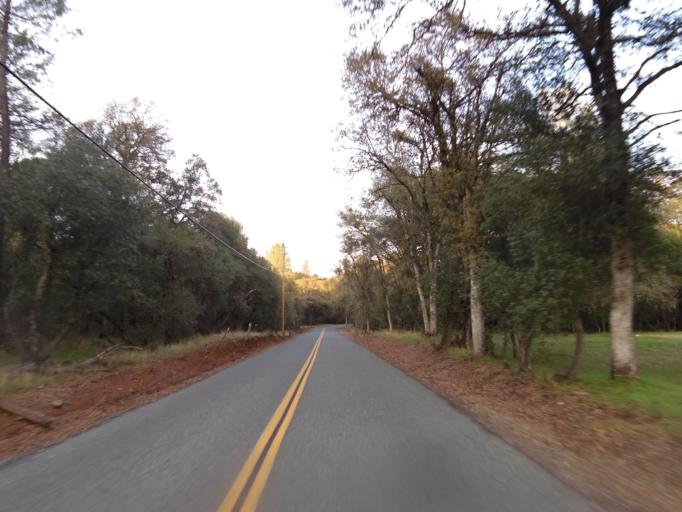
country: US
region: California
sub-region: El Dorado County
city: Cameron Park
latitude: 38.7376
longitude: -120.9969
